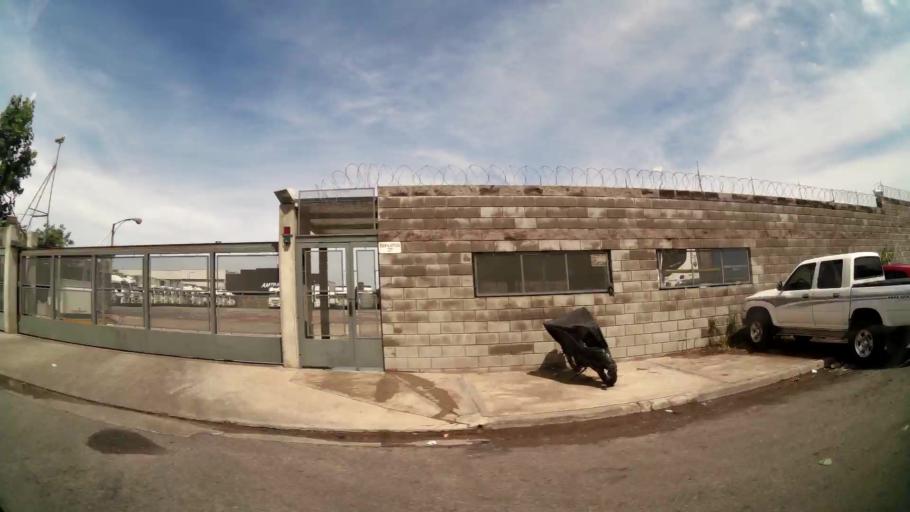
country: AR
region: Buenos Aires F.D.
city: Villa Lugano
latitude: -34.6670
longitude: -58.4374
